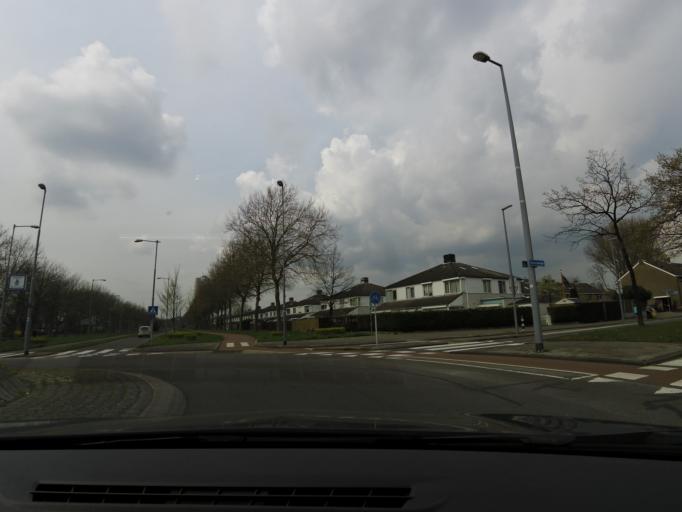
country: NL
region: South Holland
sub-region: Gemeente Spijkenisse
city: Spijkenisse
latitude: 51.8580
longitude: 4.3601
